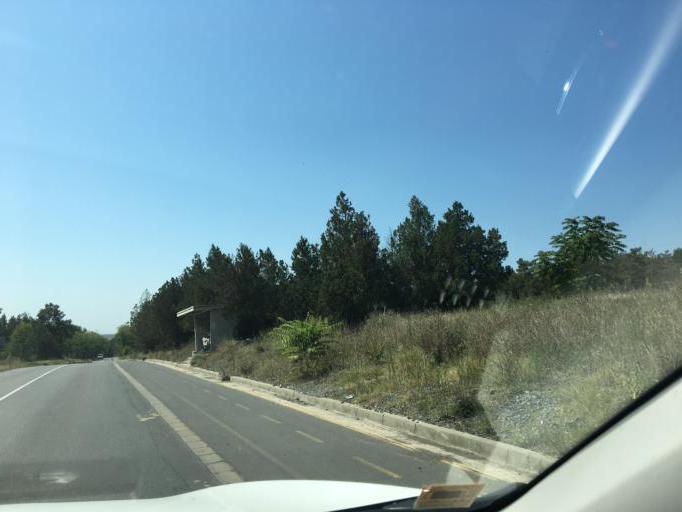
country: BG
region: Burgas
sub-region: Obshtina Kameno
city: Kameno
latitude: 42.6177
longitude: 27.3940
